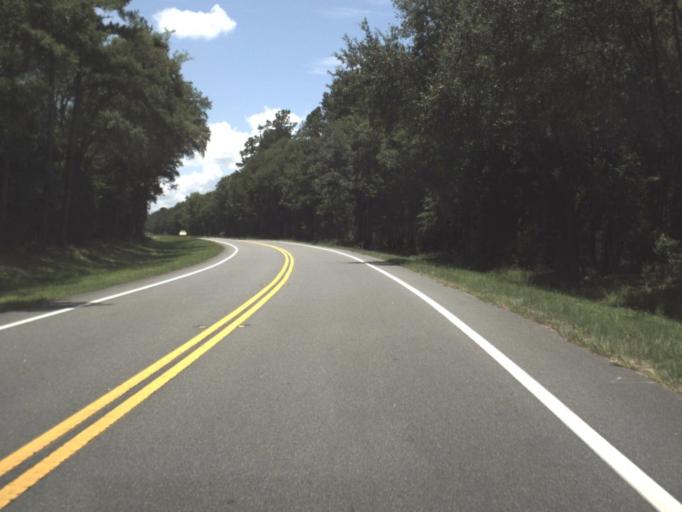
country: US
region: Florida
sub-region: Alachua County
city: Gainesville
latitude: 29.6871
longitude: -82.2416
